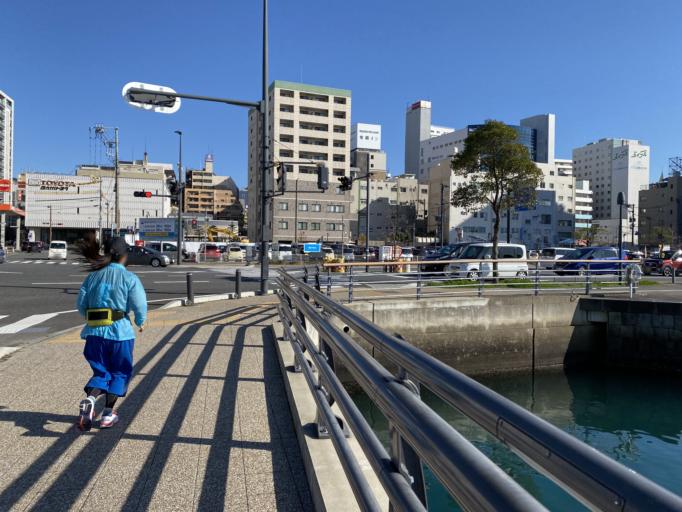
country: JP
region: Nagasaki
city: Nagasaki-shi
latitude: 32.7491
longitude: 129.8707
